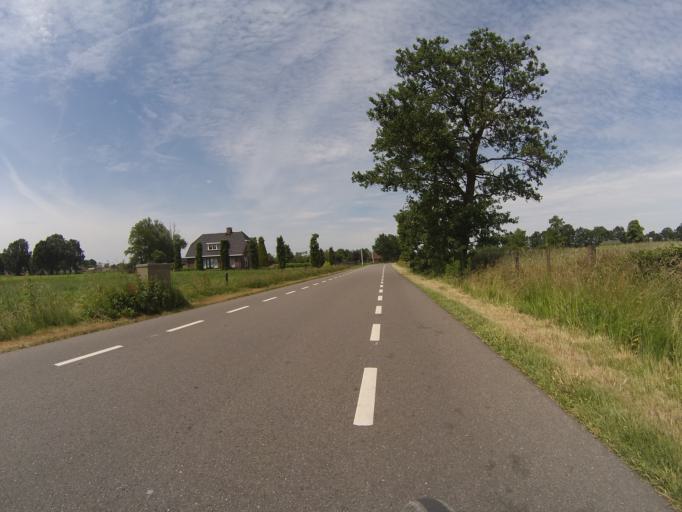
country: NL
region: Gelderland
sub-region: Gemeente Ede
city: Lunteren
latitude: 52.1154
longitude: 5.6250
